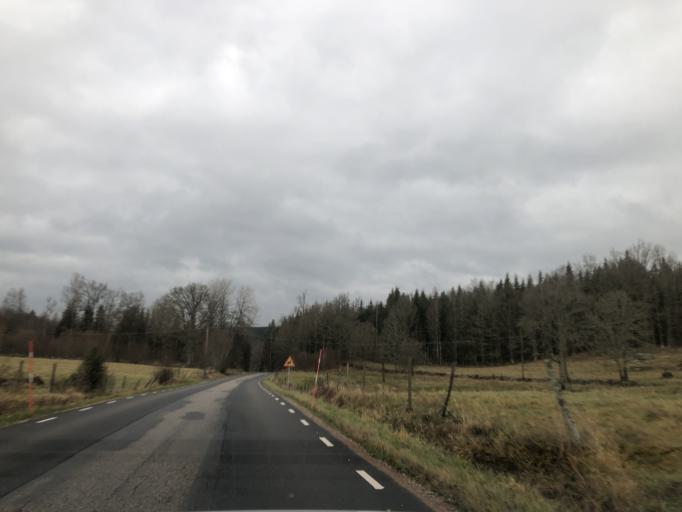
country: SE
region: Vaestra Goetaland
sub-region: Boras Kommun
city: Dalsjofors
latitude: 57.8226
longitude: 13.1939
